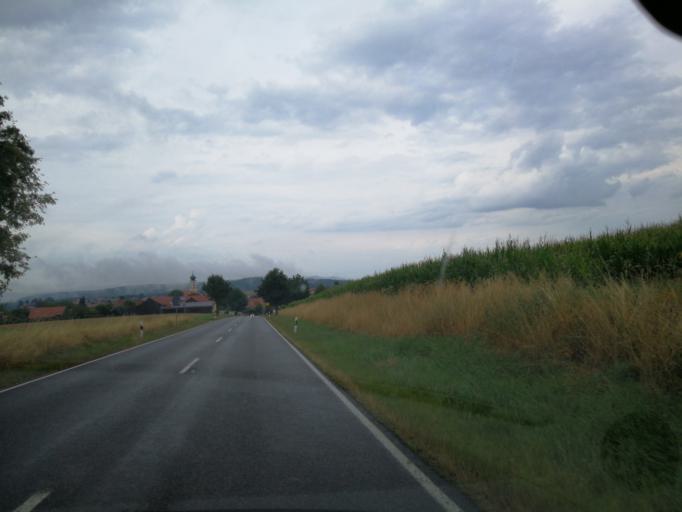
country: DE
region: Bavaria
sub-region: Upper Palatinate
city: Schorndorf
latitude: 49.1549
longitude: 12.5888
